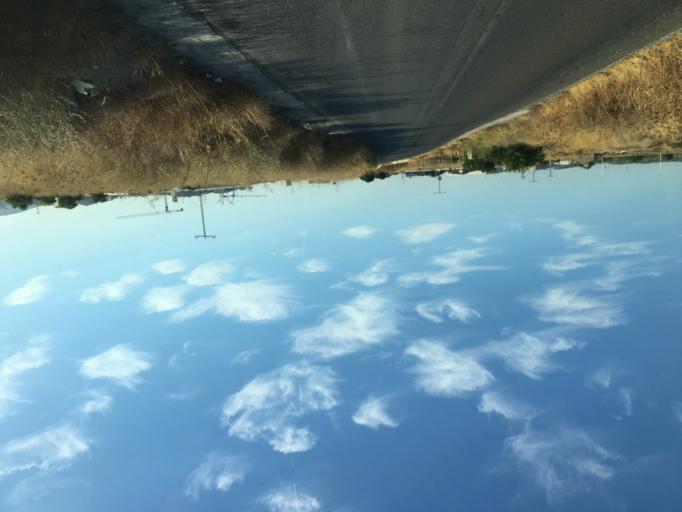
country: ES
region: Murcia
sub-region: Murcia
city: Murcia
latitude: 38.0327
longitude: -1.1205
